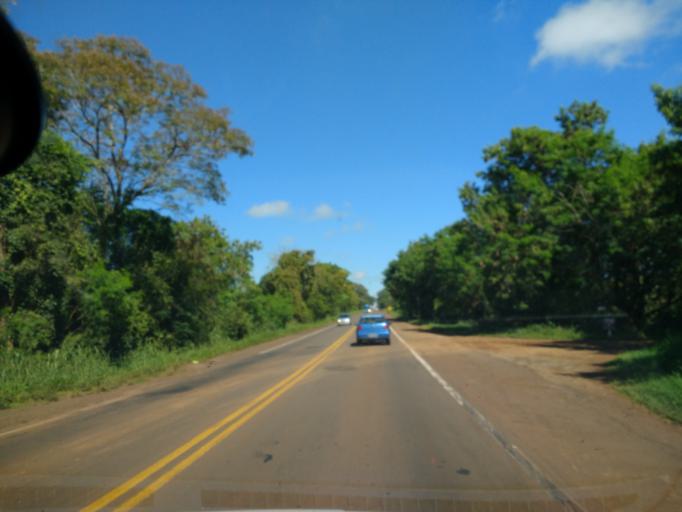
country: BR
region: Parana
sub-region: Terra Boa
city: Terra Boa
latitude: -23.6153
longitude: -52.4303
